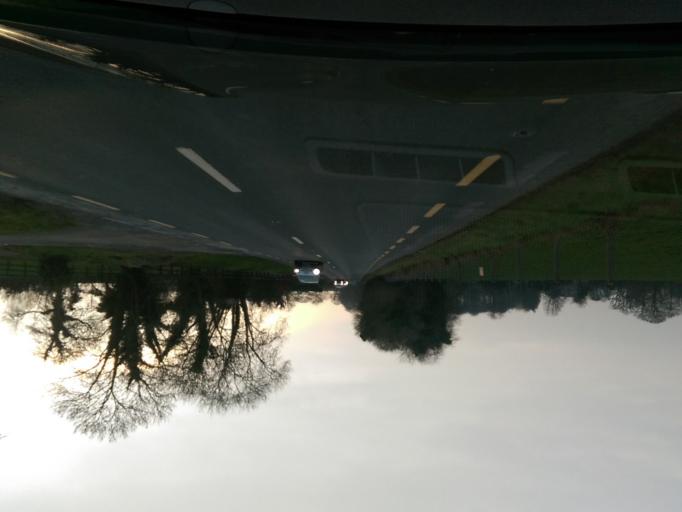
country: IE
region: Leinster
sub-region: An Longfort
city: Ballymahon
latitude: 53.5053
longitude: -7.8364
